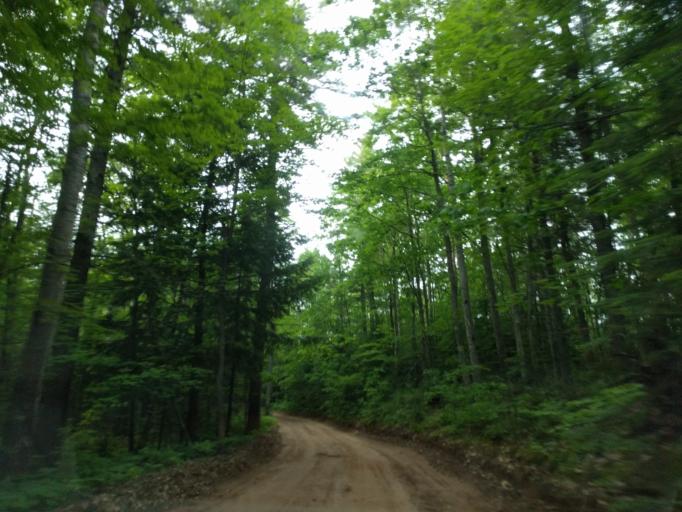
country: US
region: Michigan
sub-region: Marquette County
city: Trowbridge Park
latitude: 46.6032
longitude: -87.5000
